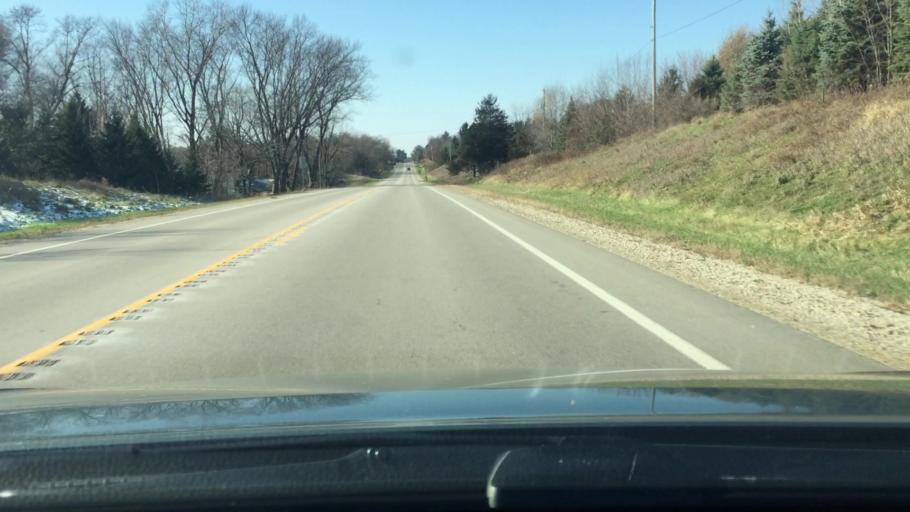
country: US
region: Wisconsin
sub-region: Jefferson County
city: Lake Ripley
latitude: 43.0118
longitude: -88.9686
